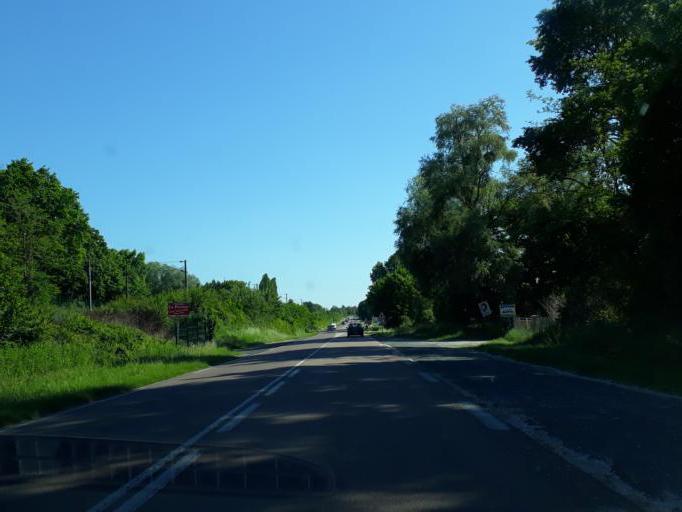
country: FR
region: Bourgogne
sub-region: Departement de la Nievre
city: Cosne-Cours-sur-Loire
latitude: 47.4292
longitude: 2.9326
